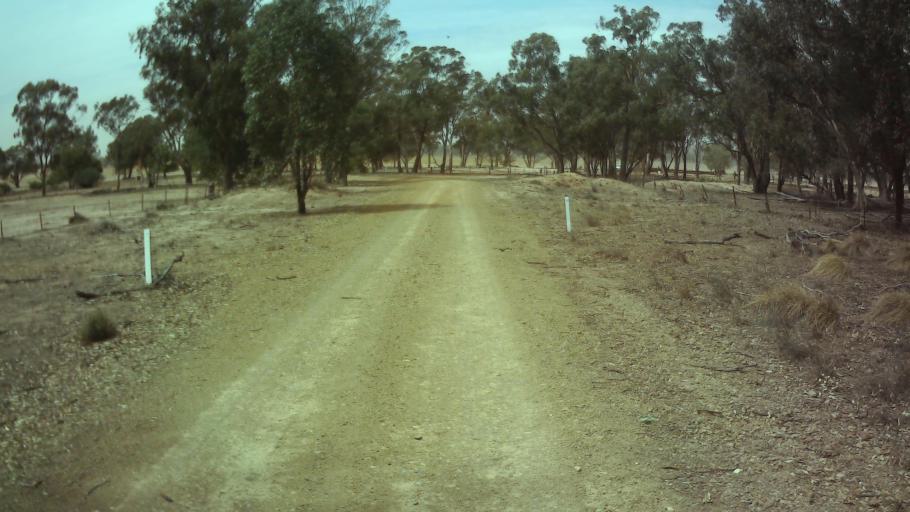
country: AU
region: New South Wales
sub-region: Weddin
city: Grenfell
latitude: -33.7423
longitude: 147.9606
